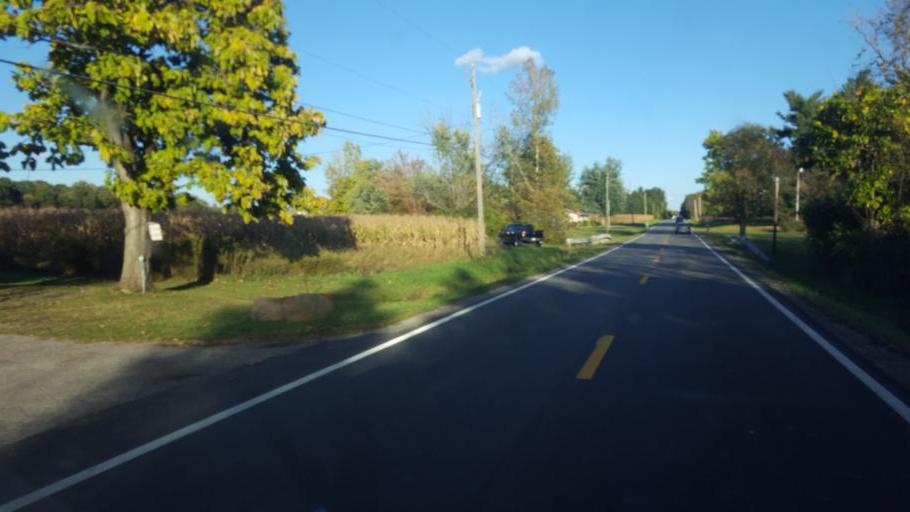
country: US
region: Ohio
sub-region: Franklin County
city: New Albany
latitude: 40.0190
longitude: -82.7850
